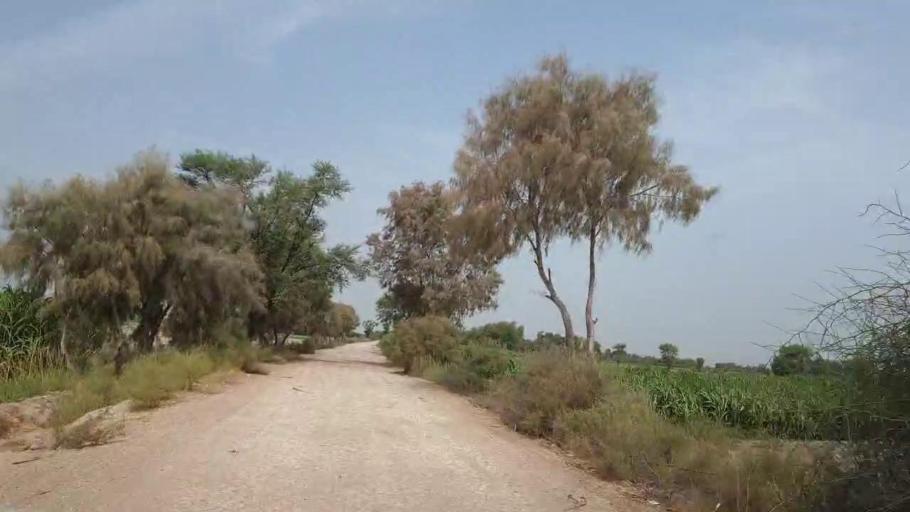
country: PK
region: Sindh
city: Sobhadero
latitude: 27.3912
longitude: 68.2681
